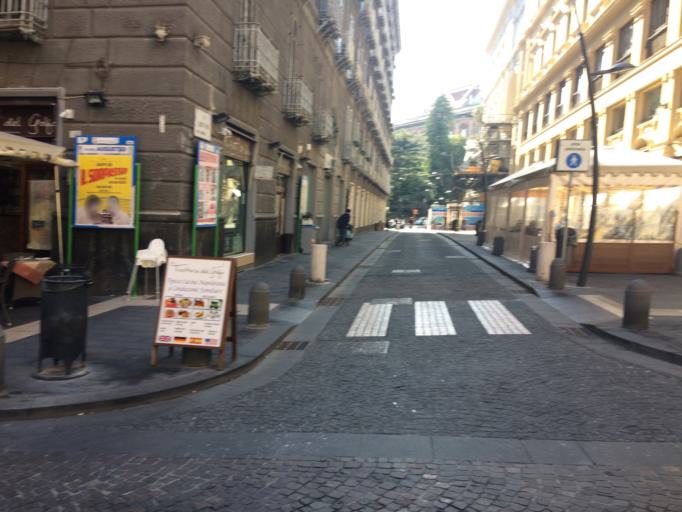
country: IT
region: Campania
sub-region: Provincia di Napoli
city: Napoli
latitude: 40.8391
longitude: 14.2505
